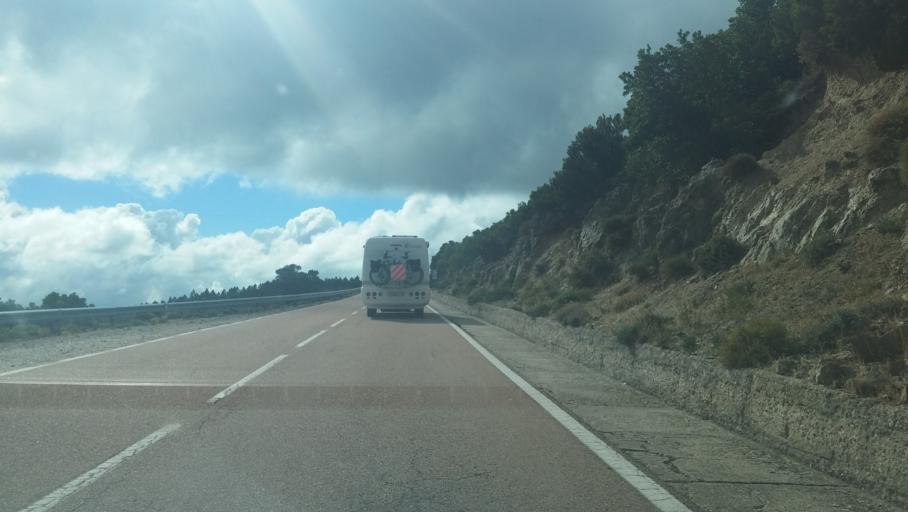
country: IT
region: Sardinia
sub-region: Provincia di Ogliastra
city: Urzulei
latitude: 40.1693
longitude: 9.5268
